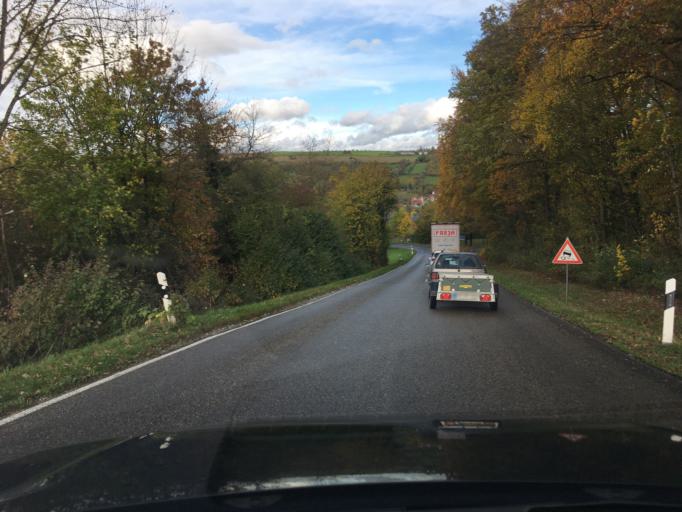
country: DE
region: Baden-Wuerttemberg
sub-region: Regierungsbezirk Stuttgart
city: Mockmuhl
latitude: 49.3164
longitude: 9.3707
